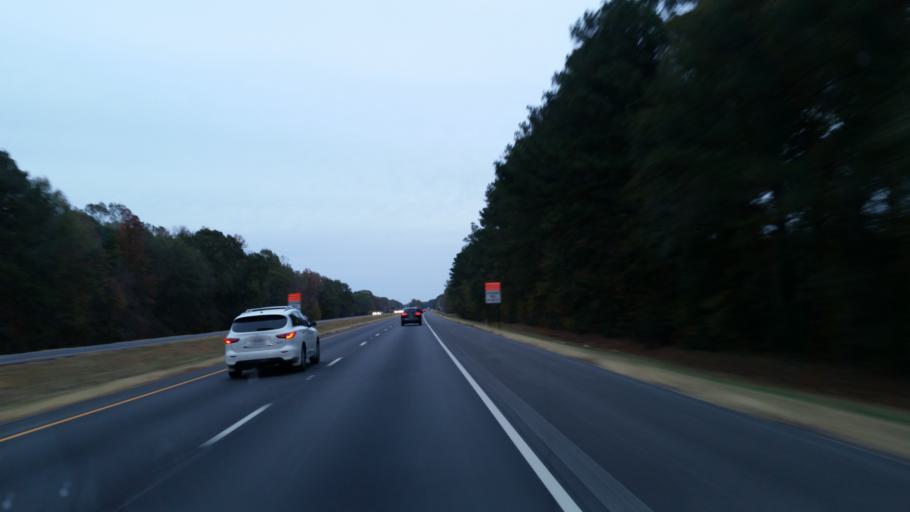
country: US
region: Alabama
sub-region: Greene County
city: Eutaw
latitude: 32.8293
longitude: -87.9789
